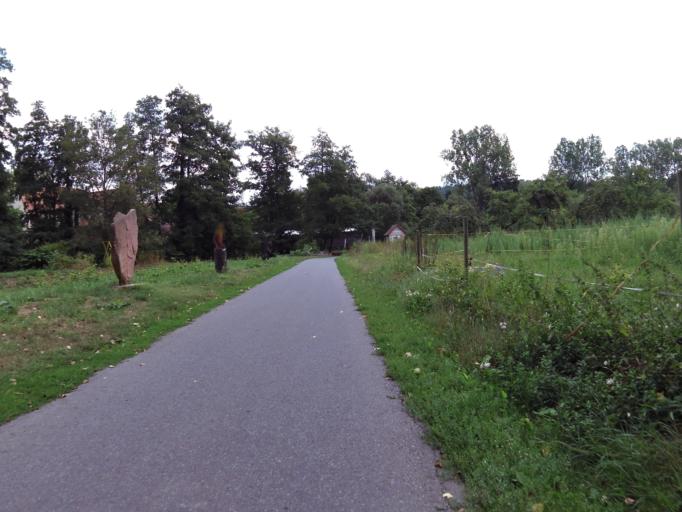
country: DE
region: Hesse
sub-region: Regierungsbezirk Darmstadt
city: Lutzelbach
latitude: 49.8163
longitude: 9.0432
